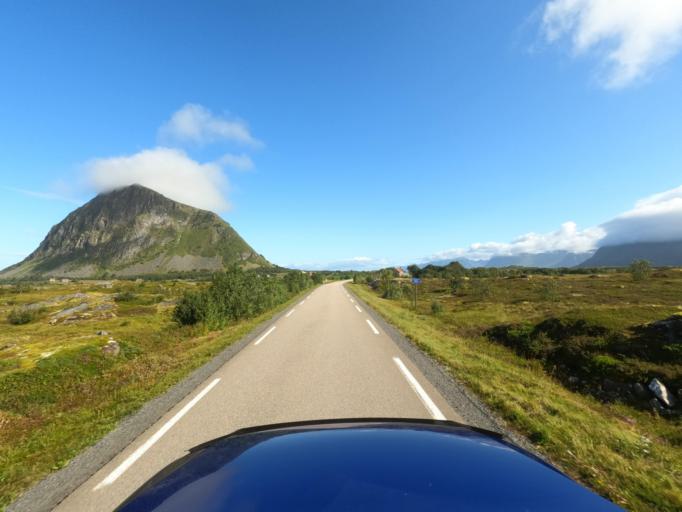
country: NO
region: Nordland
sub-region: Vestvagoy
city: Evjen
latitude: 68.3181
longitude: 14.0952
